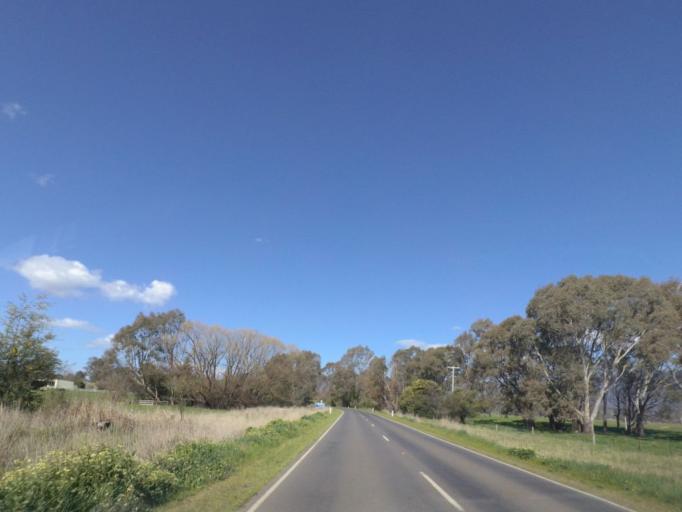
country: AU
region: Victoria
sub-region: Murrindindi
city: Alexandra
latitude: -37.2533
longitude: 145.7890
